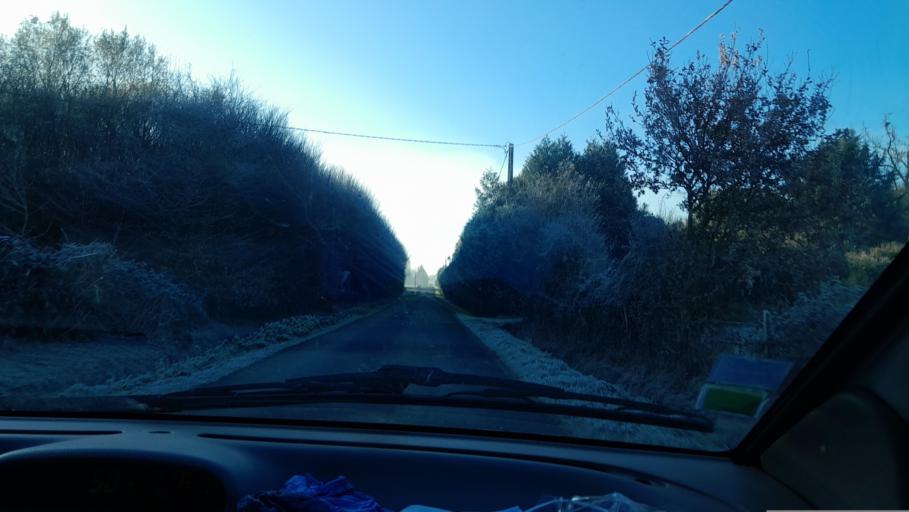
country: FR
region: Brittany
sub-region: Departement d'Ille-et-Vilaine
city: La Guerche-de-Bretagne
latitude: 47.9009
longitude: -1.1612
